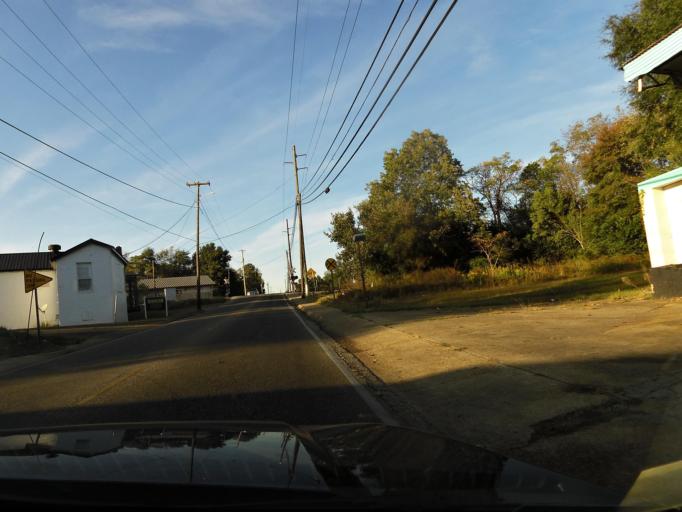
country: US
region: Alabama
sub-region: Houston County
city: Dothan
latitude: 31.2314
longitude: -85.3830
